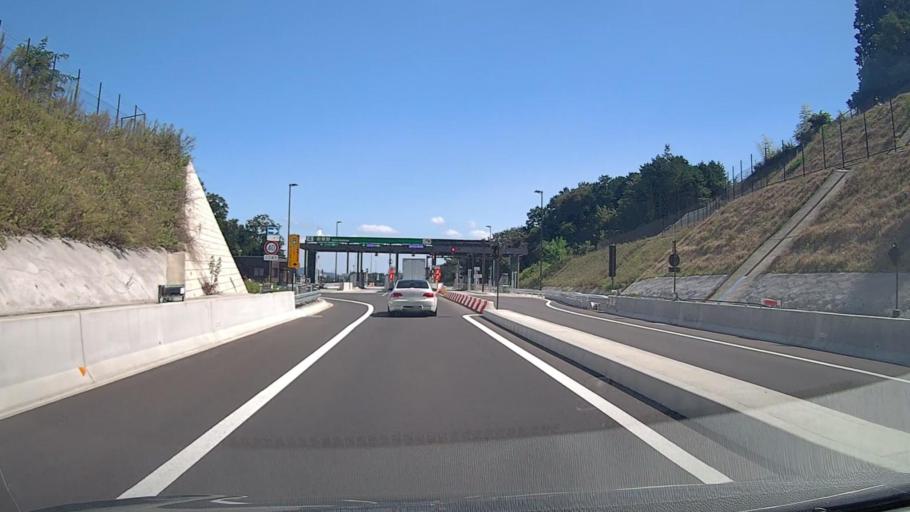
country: JP
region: Kanagawa
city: Hadano
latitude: 35.3730
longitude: 139.1579
